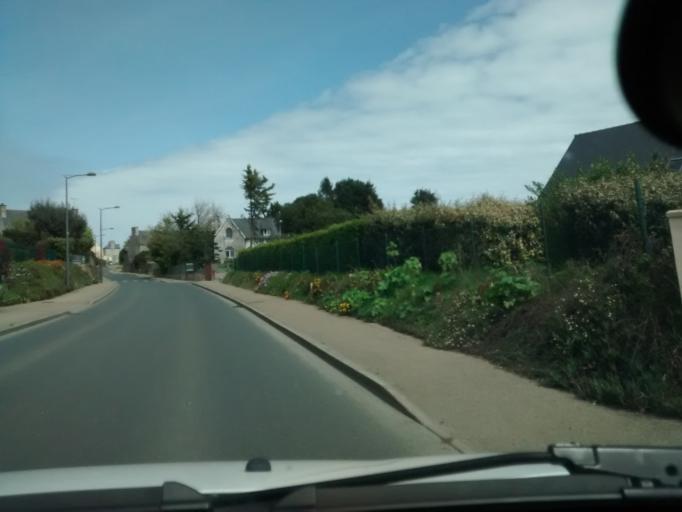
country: FR
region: Brittany
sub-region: Departement des Cotes-d'Armor
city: Ploubazlanec
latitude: 48.7975
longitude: -3.0341
